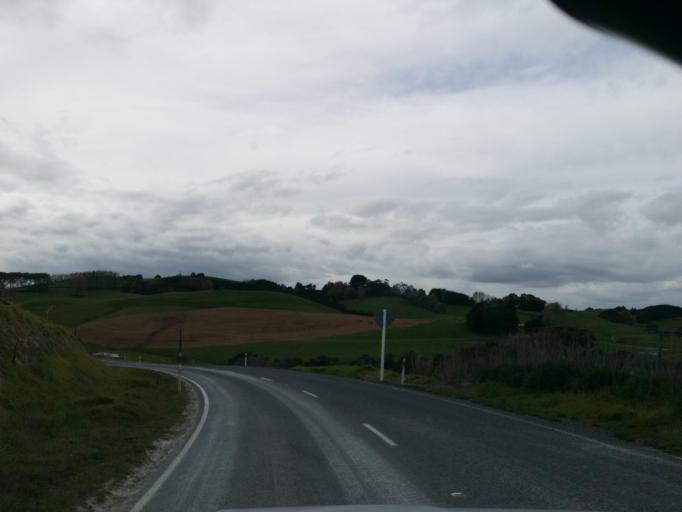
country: NZ
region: Northland
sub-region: Kaipara District
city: Dargaville
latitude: -35.9681
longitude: 173.9353
